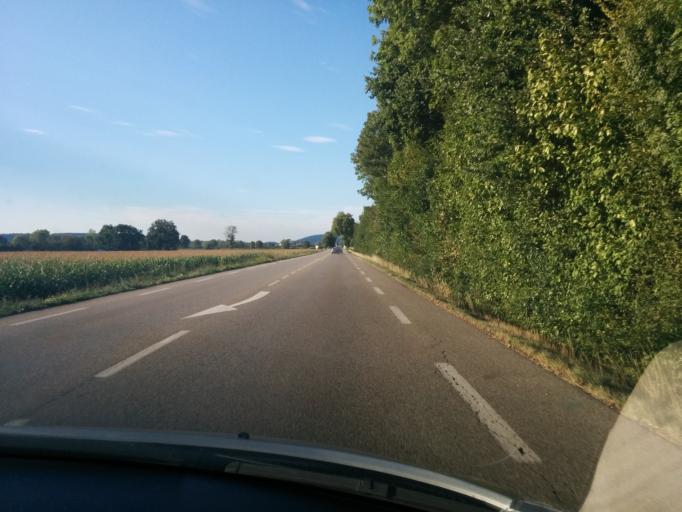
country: FR
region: Rhone-Alpes
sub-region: Departement de l'Ain
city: Ambronay
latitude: 45.9990
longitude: 5.3423
